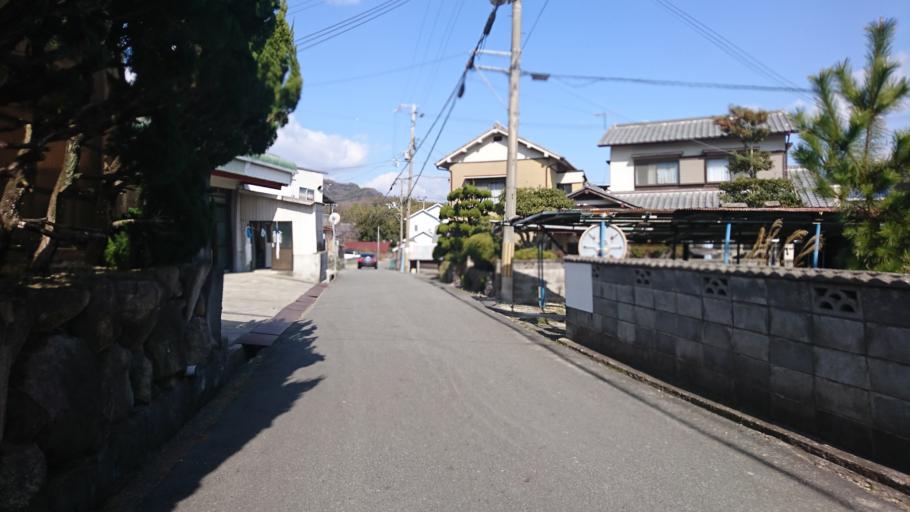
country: JP
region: Hyogo
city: Kakogawacho-honmachi
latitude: 34.8172
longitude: 134.8024
